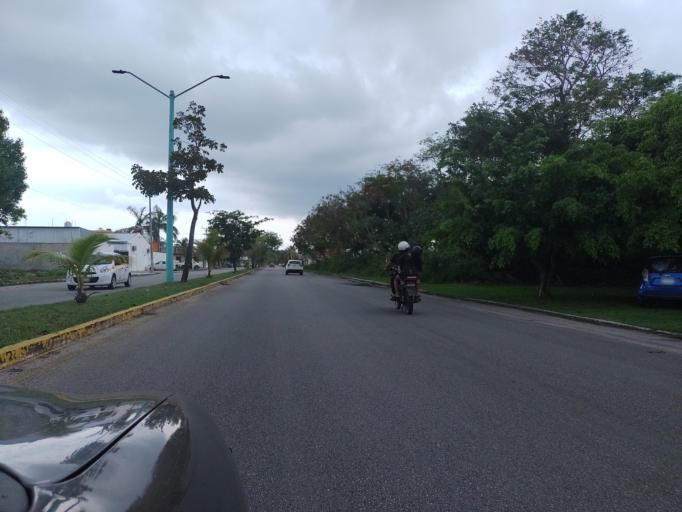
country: MX
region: Quintana Roo
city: Chetumal
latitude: 18.5066
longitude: -88.2841
